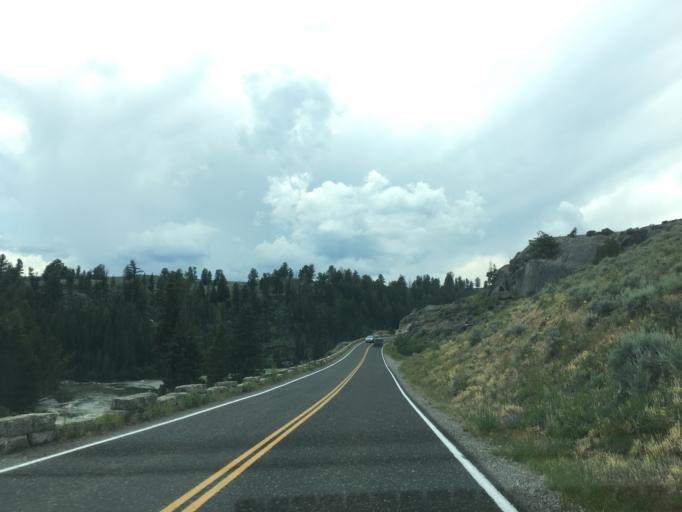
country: US
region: Montana
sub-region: Park County
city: Livingston
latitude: 44.9146
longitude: -110.2788
